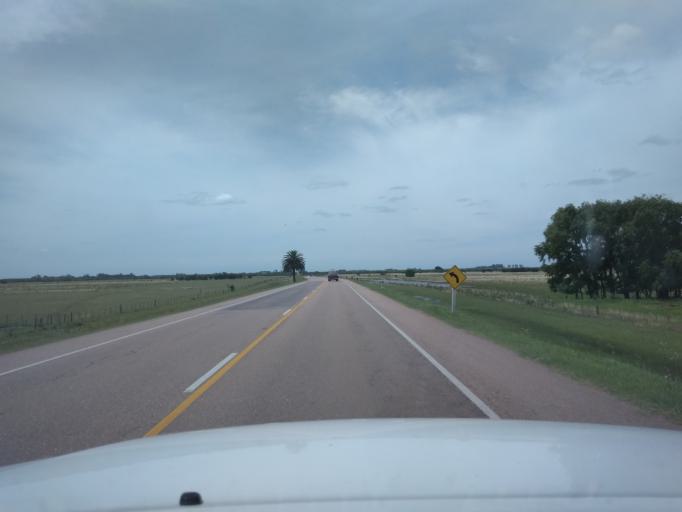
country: UY
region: Canelones
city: Canelones
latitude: -34.3853
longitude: -56.2533
